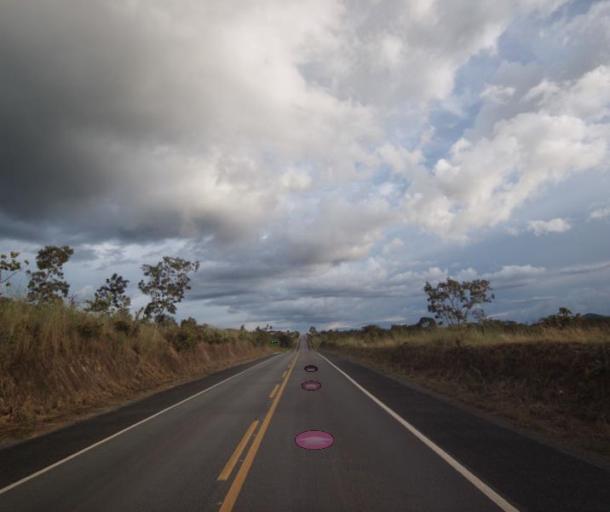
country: BR
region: Goias
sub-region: Barro Alto
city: Barro Alto
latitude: -14.8634
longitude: -48.6395
